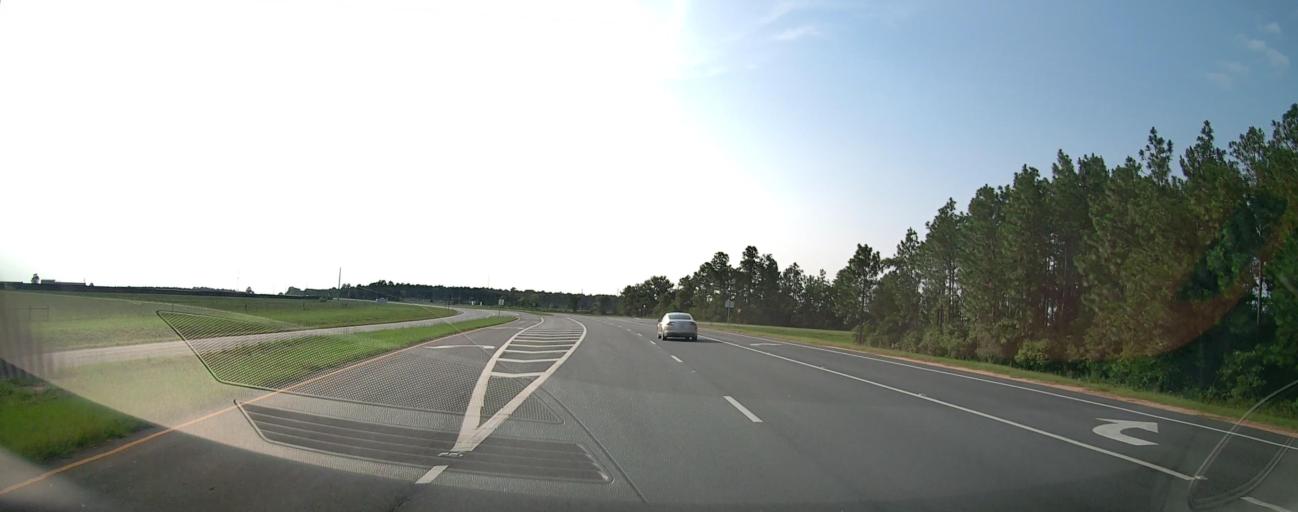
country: US
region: Georgia
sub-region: Taylor County
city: Butler
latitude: 32.5654
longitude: -84.2696
